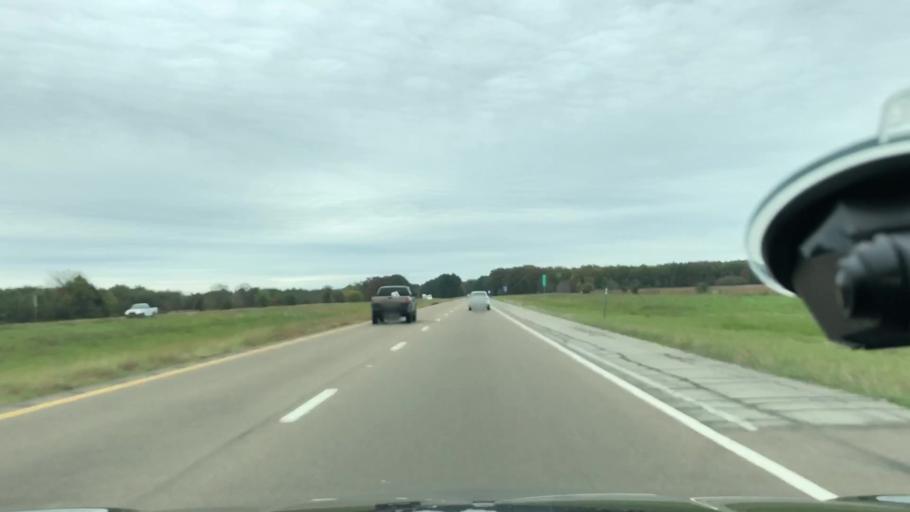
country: US
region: Texas
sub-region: Morris County
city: Naples
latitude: 33.2950
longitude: -94.7297
